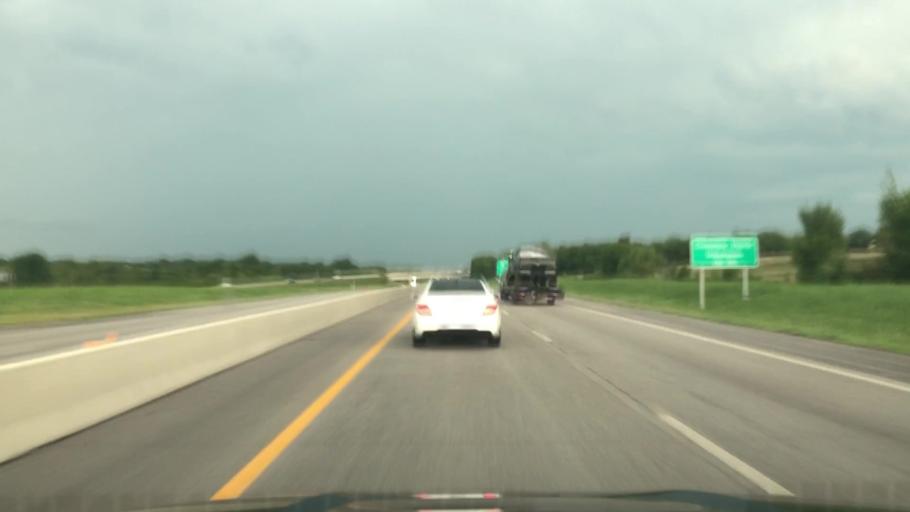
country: US
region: Oklahoma
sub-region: Rogers County
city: Justice
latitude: 36.3096
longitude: -95.5723
